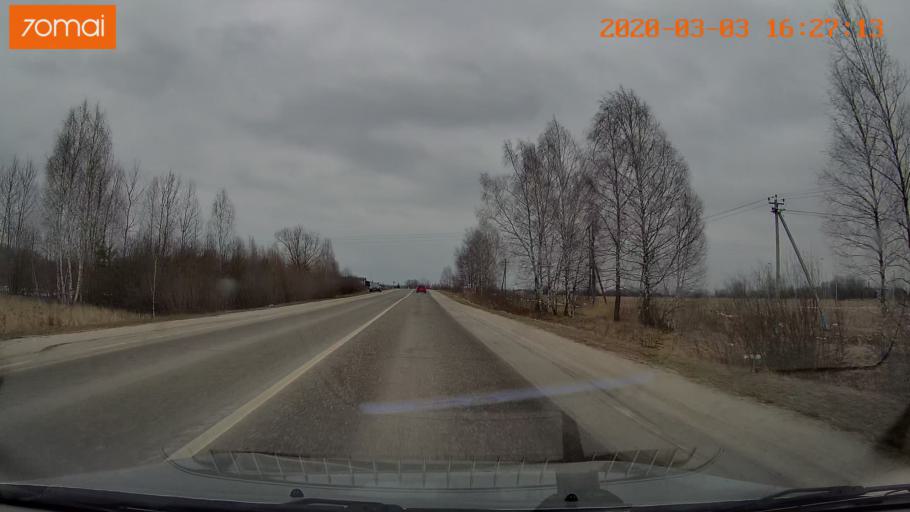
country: RU
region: Moskovskaya
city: Konobeyevo
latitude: 55.4360
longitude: 38.6679
